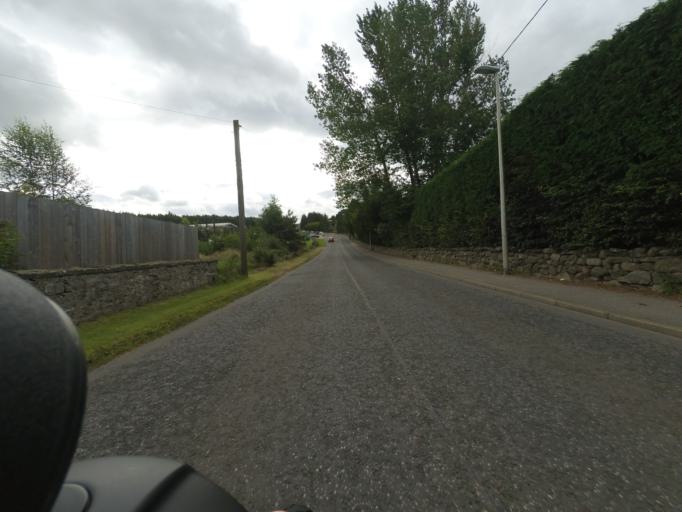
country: GB
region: Scotland
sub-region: Aberdeenshire
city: Banchory
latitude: 57.0629
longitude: -2.4964
